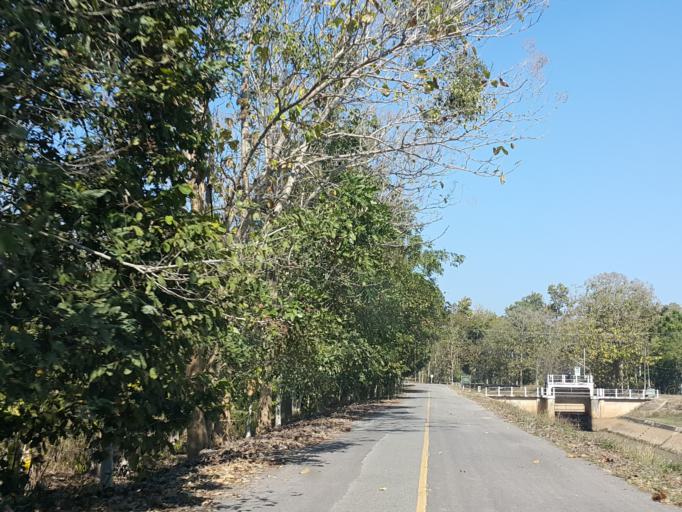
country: TH
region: Chiang Mai
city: Mae Taeng
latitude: 19.0967
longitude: 98.9522
